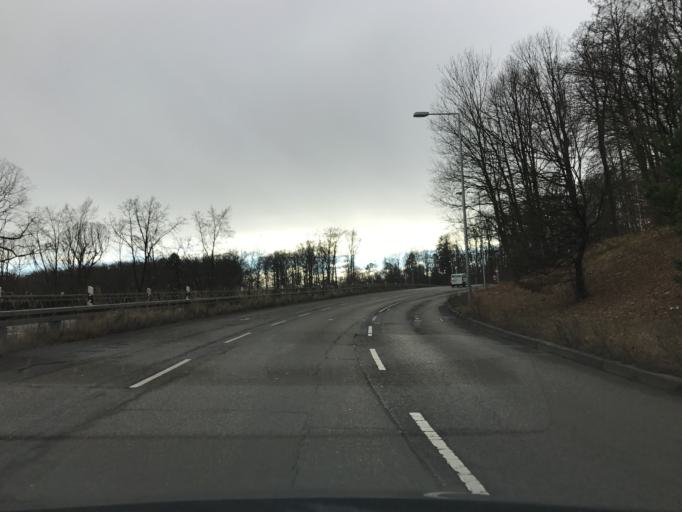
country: DE
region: Baden-Wuerttemberg
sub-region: Regierungsbezirk Stuttgart
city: Stuttgart-Ost
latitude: 48.7579
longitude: 9.1948
